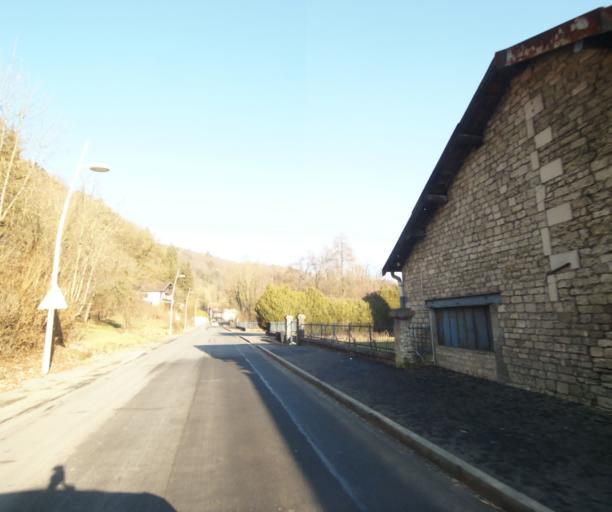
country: FR
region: Champagne-Ardenne
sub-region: Departement de la Haute-Marne
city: Chevillon
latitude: 48.5269
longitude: 5.1235
